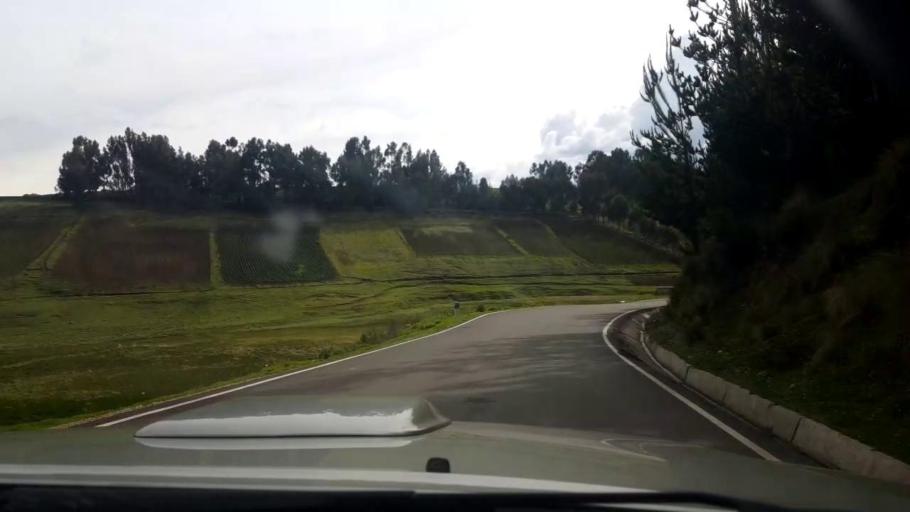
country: PE
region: Ayacucho
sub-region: Provincia de Cangallo
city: Pampa Cangallo
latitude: -13.4507
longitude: -74.2029
